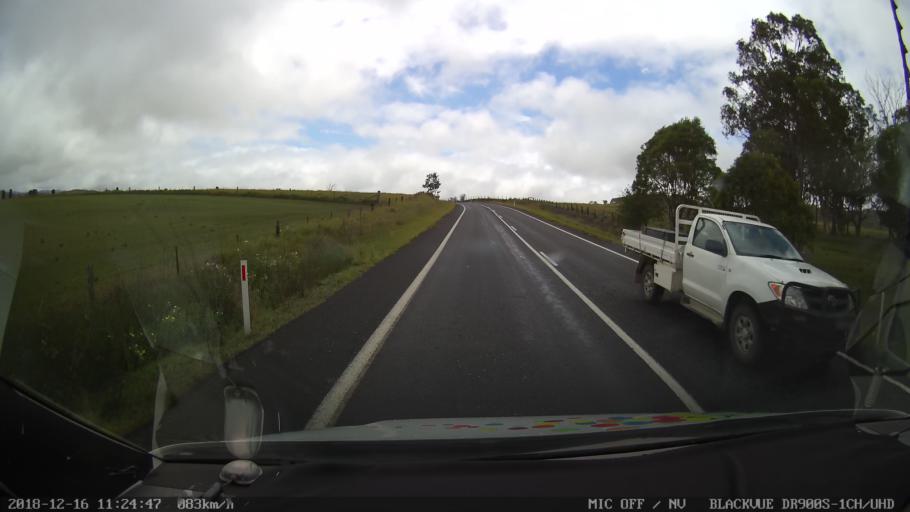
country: AU
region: New South Wales
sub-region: Tenterfield Municipality
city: Carrolls Creek
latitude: -29.0584
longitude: 152.0527
